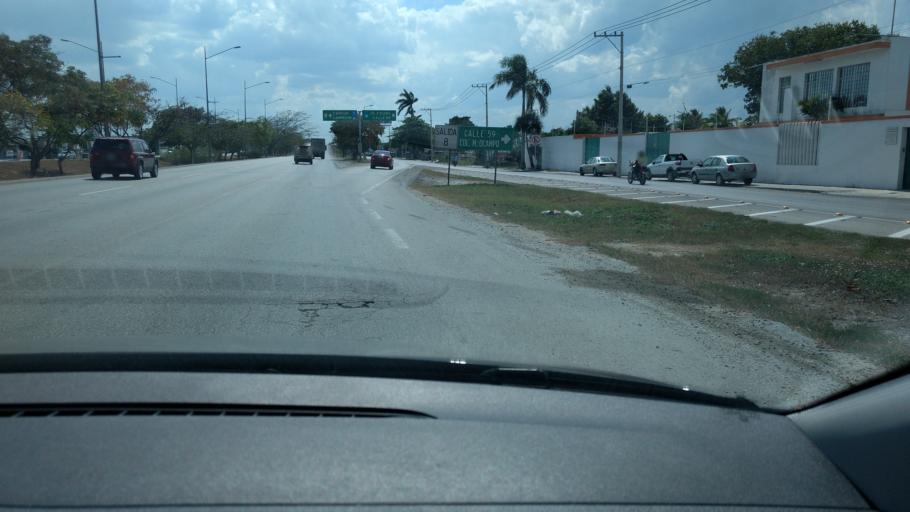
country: MX
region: Yucatan
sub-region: Kanasin
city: Kanasin
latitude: 20.9729
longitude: -89.5653
